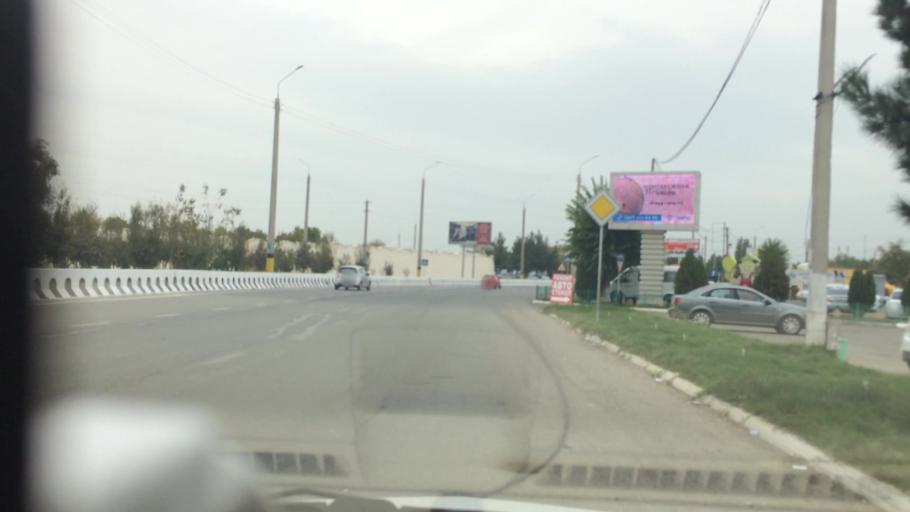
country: UZ
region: Toshkent
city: Salor
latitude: 41.3088
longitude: 69.3435
